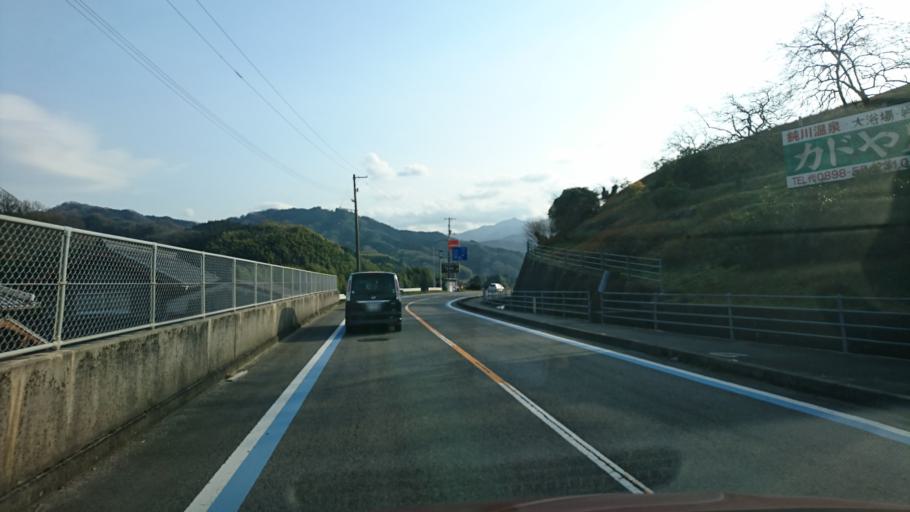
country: JP
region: Ehime
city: Hojo
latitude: 34.0055
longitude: 132.9386
